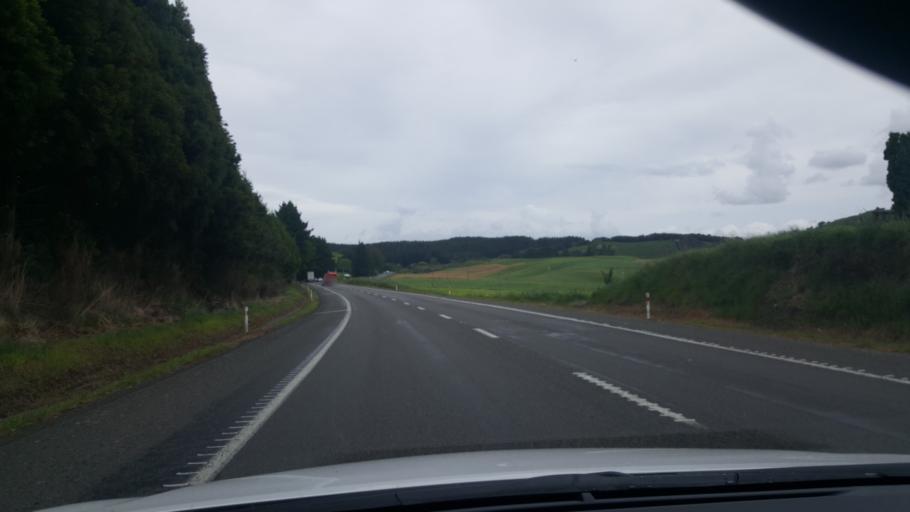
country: NZ
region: Bay of Plenty
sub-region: Rotorua District
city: Rotorua
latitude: -38.2705
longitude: 176.3337
